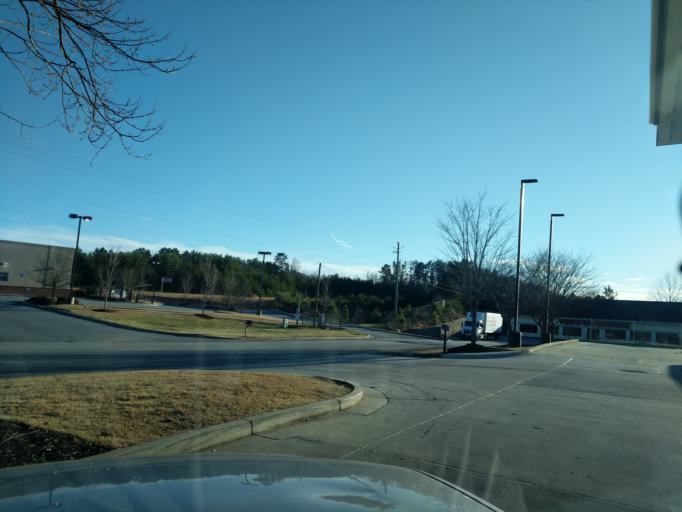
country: US
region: Georgia
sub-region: Habersham County
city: Demorest
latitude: 34.5432
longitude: -83.5448
